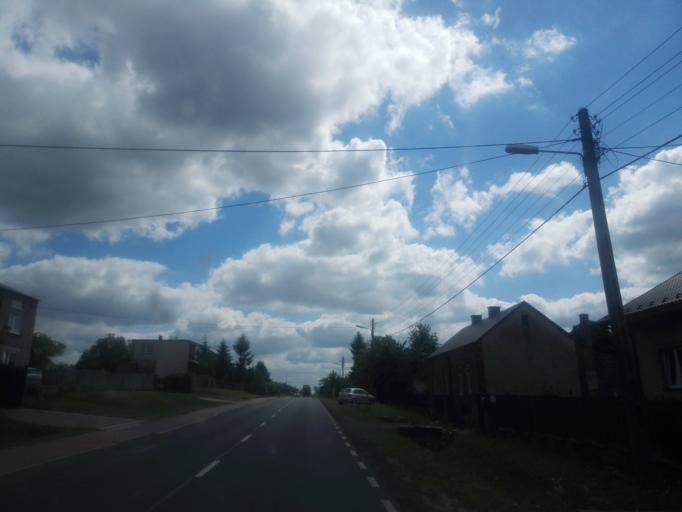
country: PL
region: Silesian Voivodeship
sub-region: Powiat czestochowski
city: Mstow
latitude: 50.7973
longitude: 19.2643
